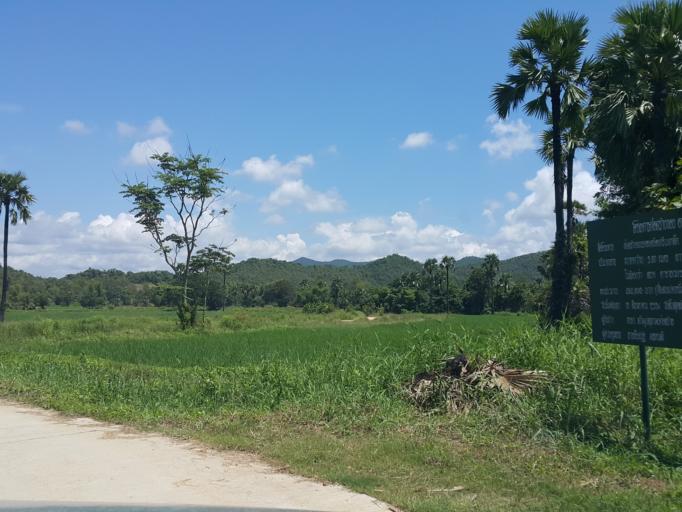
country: TH
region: Lamphun
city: Ban Thi
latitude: 18.6688
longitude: 99.1571
